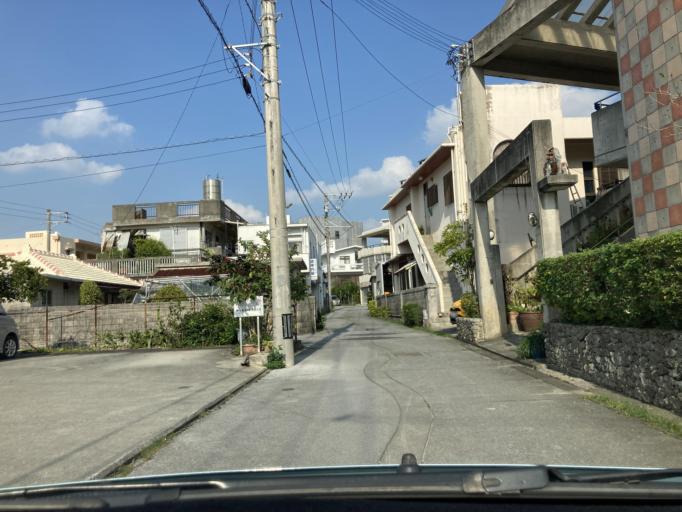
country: JP
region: Okinawa
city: Tomigusuku
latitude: 26.1886
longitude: 127.7264
